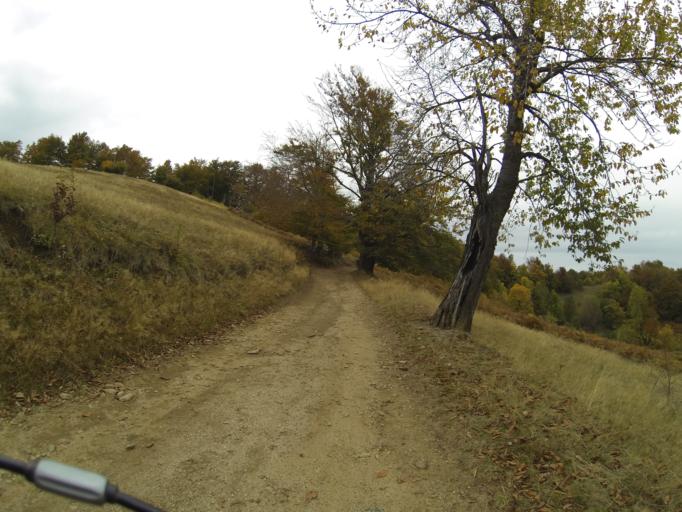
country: RO
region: Gorj
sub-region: Comuna Pades
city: Closani
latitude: 45.0919
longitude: 22.8384
